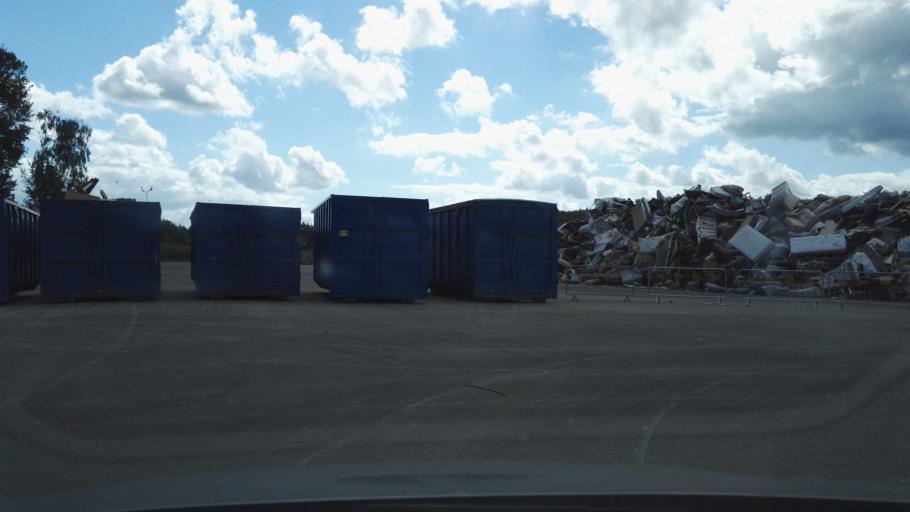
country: SE
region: Kronoberg
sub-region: Vaxjo Kommun
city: Gemla
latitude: 56.8560
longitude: 14.6930
